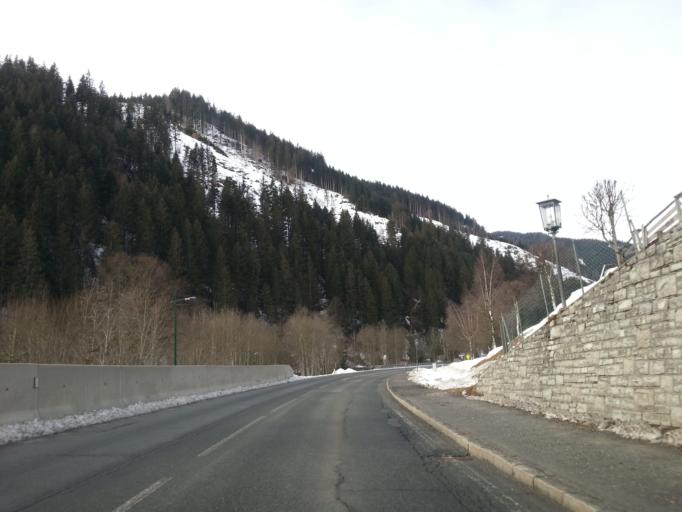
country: AT
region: Salzburg
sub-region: Politischer Bezirk Zell am See
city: Viehhofen
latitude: 47.3660
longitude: 12.7203
